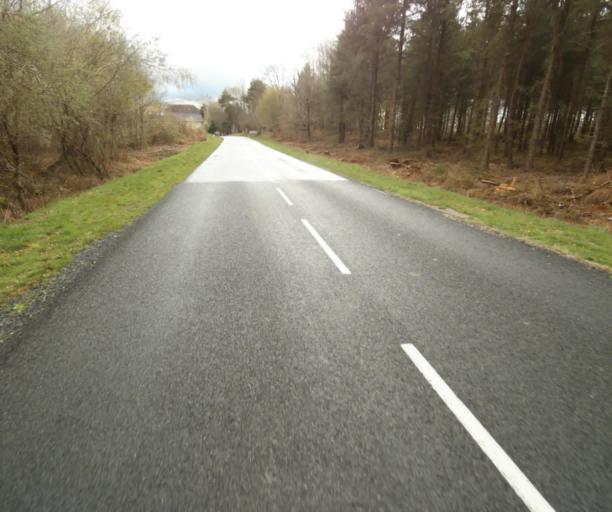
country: FR
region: Limousin
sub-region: Departement de la Correze
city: Saint-Privat
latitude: 45.2258
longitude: 2.0076
